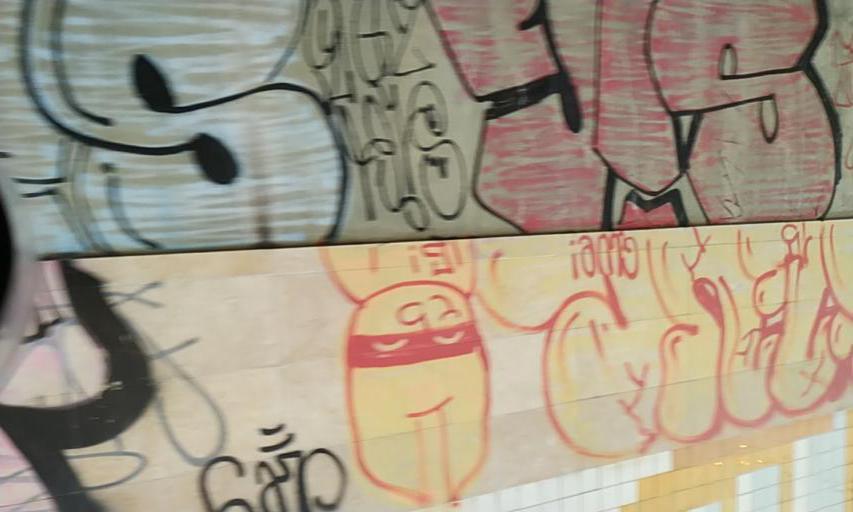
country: PT
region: Setubal
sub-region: Setubal
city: Setubal
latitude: 38.5299
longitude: -8.8850
